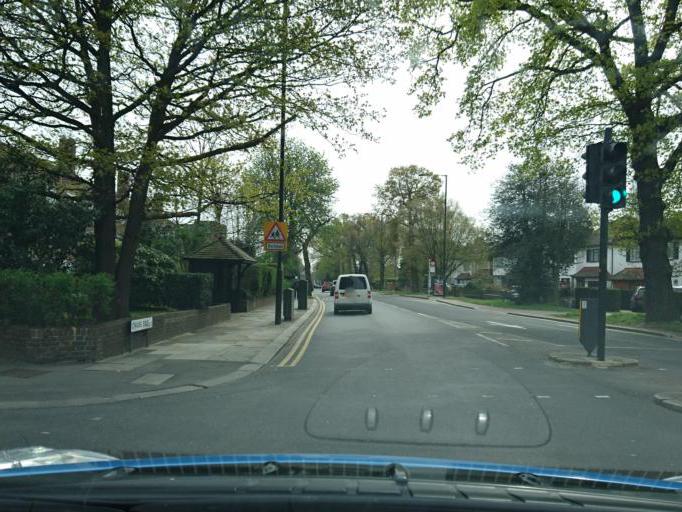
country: GB
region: England
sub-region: Greater London
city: Wood Green
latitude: 51.6367
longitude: -0.1383
